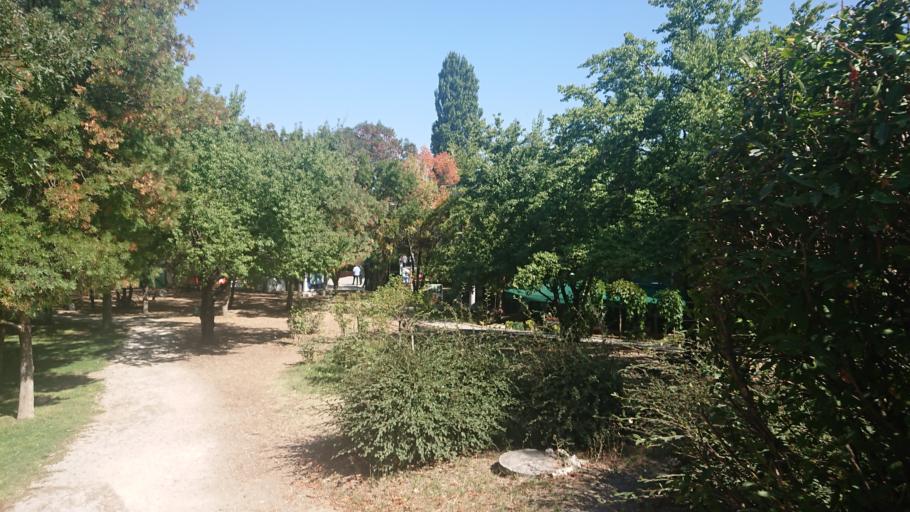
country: TR
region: Ankara
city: Ankara
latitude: 39.8922
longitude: 32.7874
